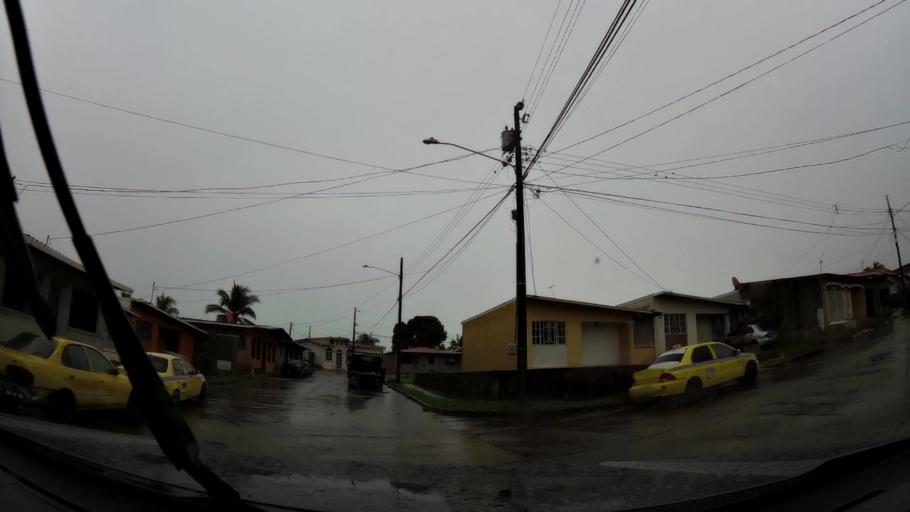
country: PA
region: Colon
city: Puerto Pilon
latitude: 9.3551
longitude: -79.7949
